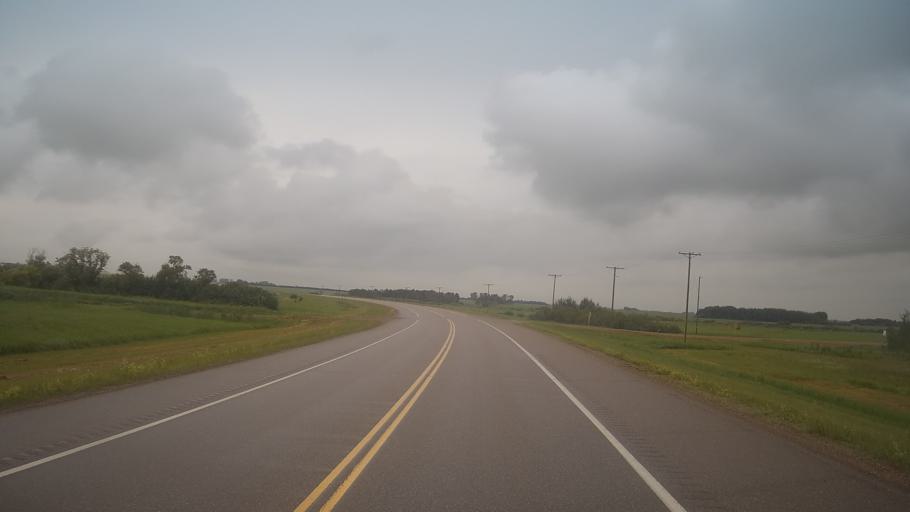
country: CA
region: Saskatchewan
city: Wilkie
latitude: 52.4337
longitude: -108.9281
